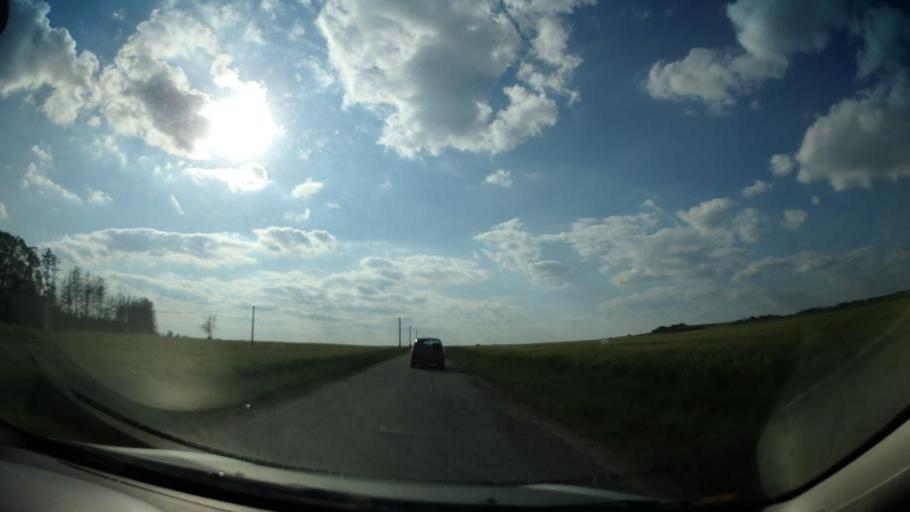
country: CZ
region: Vysocina
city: Vladislav
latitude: 49.2183
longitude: 16.0185
